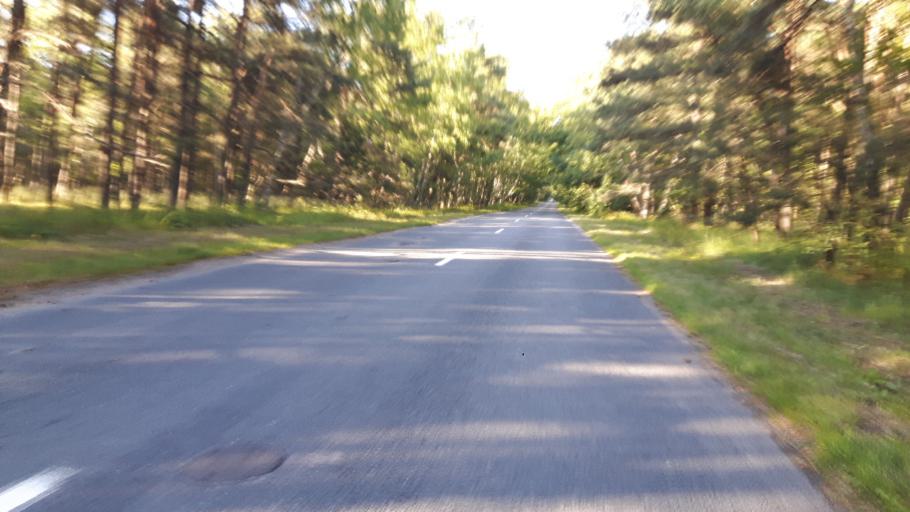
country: LT
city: Nida
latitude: 55.2263
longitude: 20.8966
